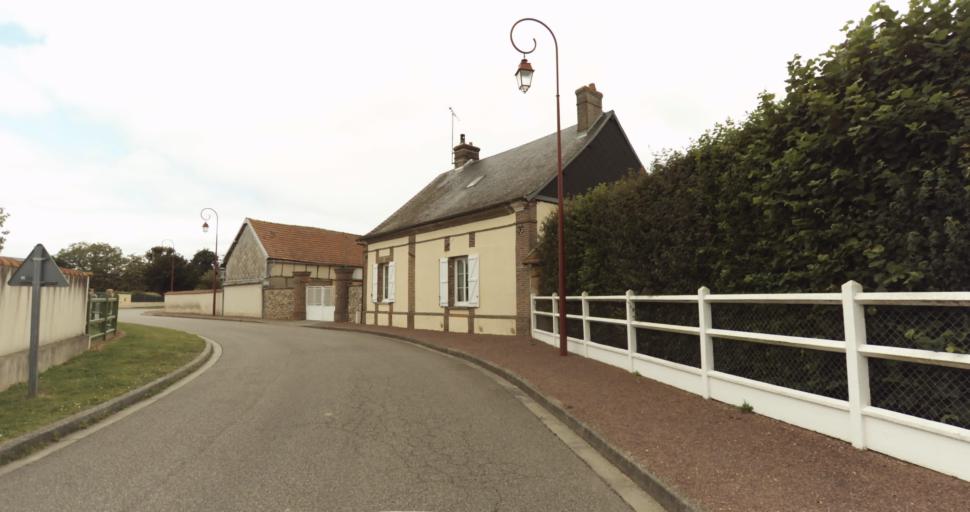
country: FR
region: Haute-Normandie
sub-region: Departement de l'Eure
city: Evreux
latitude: 48.9372
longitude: 1.1964
